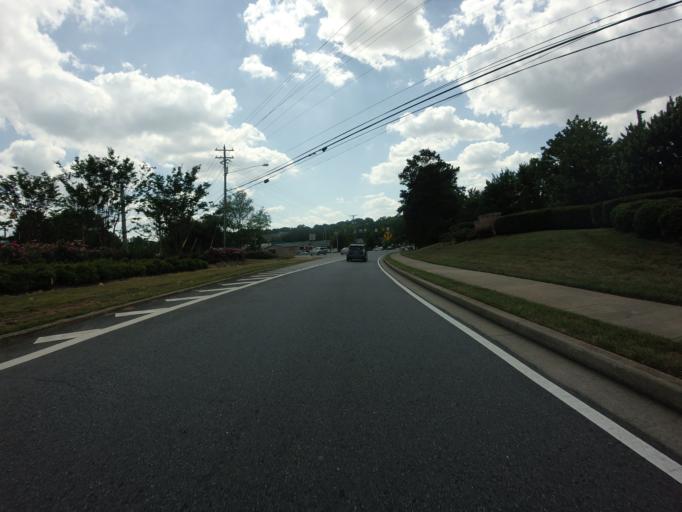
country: US
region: Georgia
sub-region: Fulton County
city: Alpharetta
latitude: 34.0200
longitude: -84.2768
